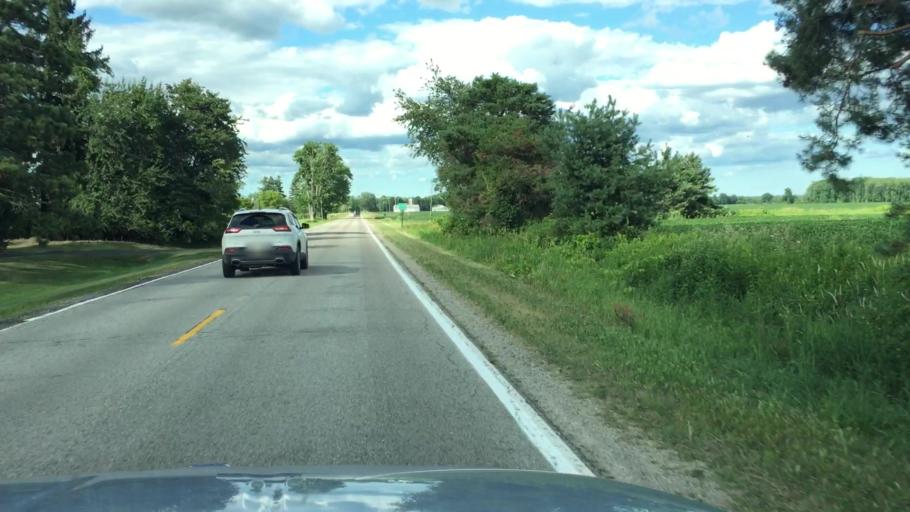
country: US
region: Michigan
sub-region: Saint Clair County
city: Capac
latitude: 43.0690
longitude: -82.9264
